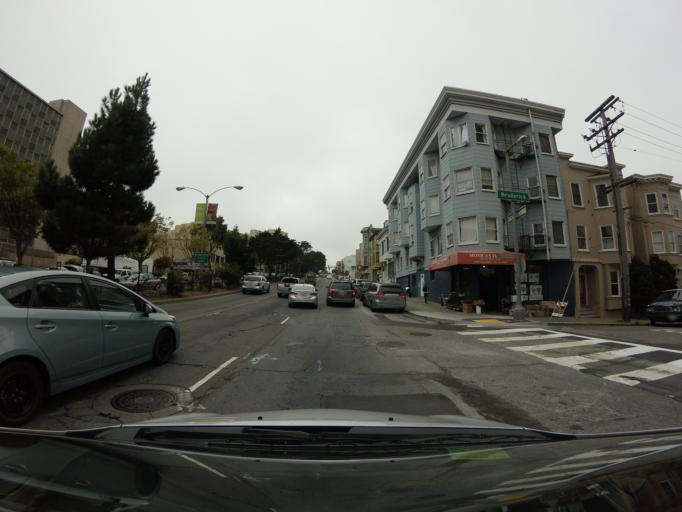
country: US
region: California
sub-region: San Francisco County
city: San Francisco
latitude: 37.7832
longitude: -122.4411
